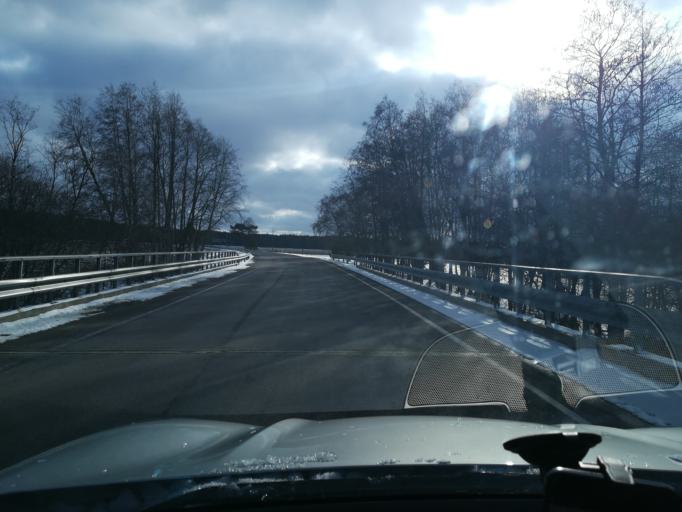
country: EE
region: Harju
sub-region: Keila linn
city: Keila
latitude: 59.4124
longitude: 24.4115
